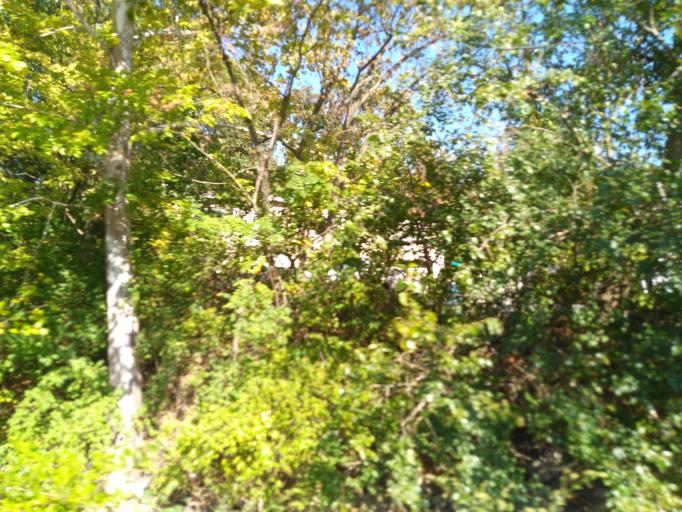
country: US
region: Missouri
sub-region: Saint Louis County
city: Green Park
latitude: 38.5008
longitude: -90.3489
